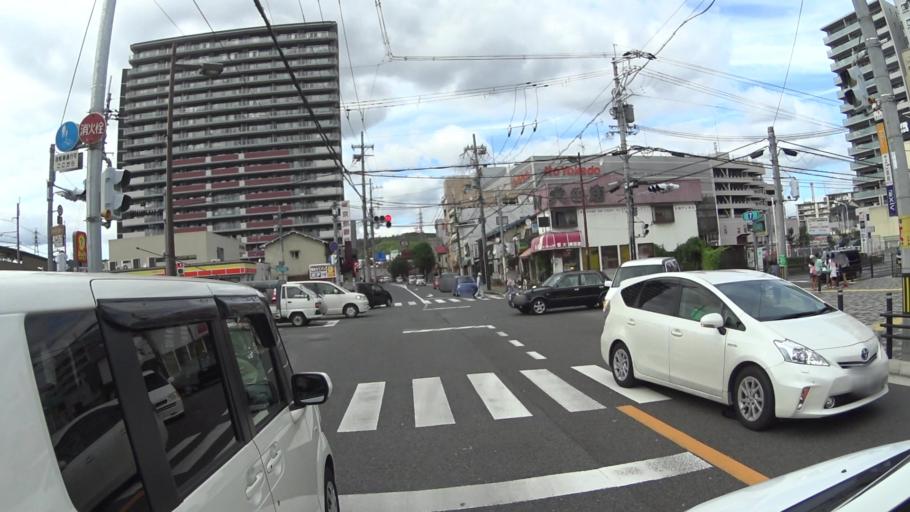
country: JP
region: Kyoto
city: Uji
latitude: 34.9326
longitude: 135.7985
